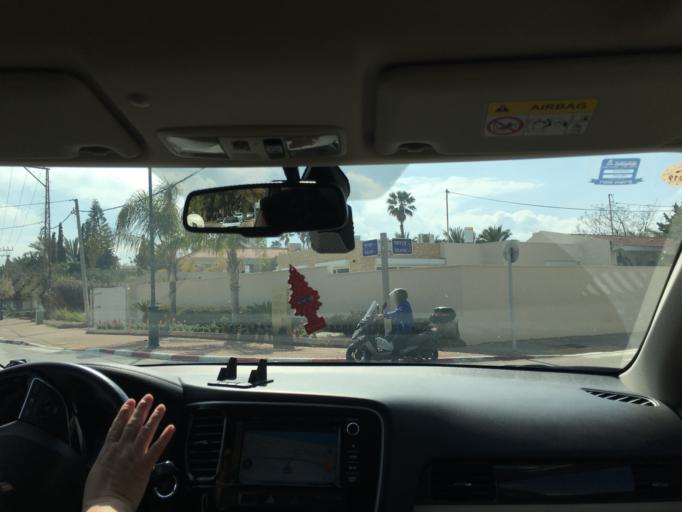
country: IL
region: Tel Aviv
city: Herzliya Pituah
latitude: 32.1815
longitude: 34.8070
